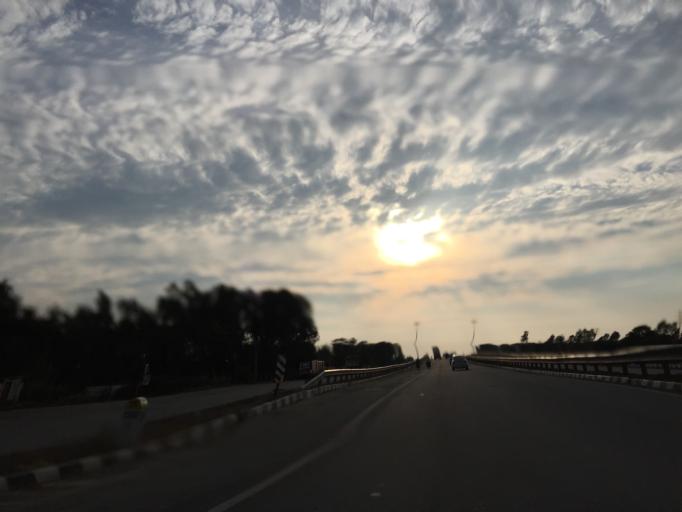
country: IN
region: Karnataka
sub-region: Kolar
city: Kolar
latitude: 13.1428
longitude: 78.2345
